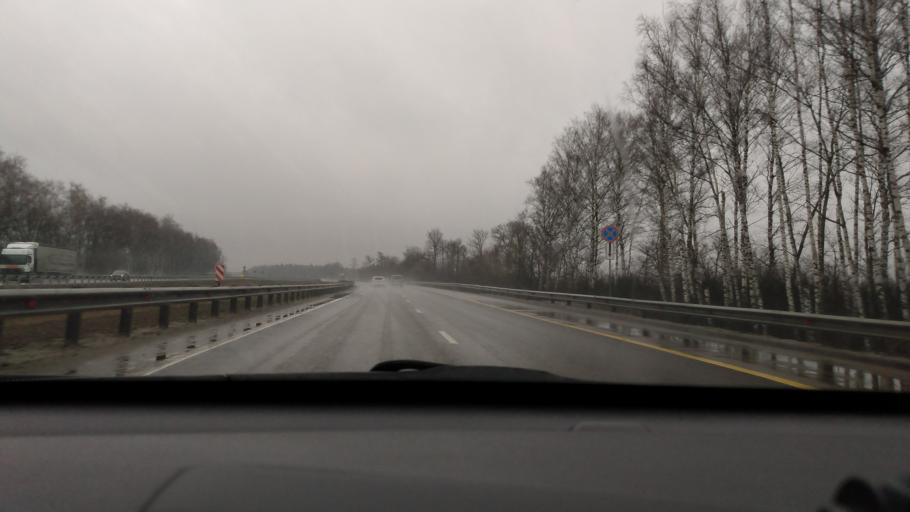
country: RU
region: Tula
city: Venev
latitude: 54.4663
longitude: 38.1739
